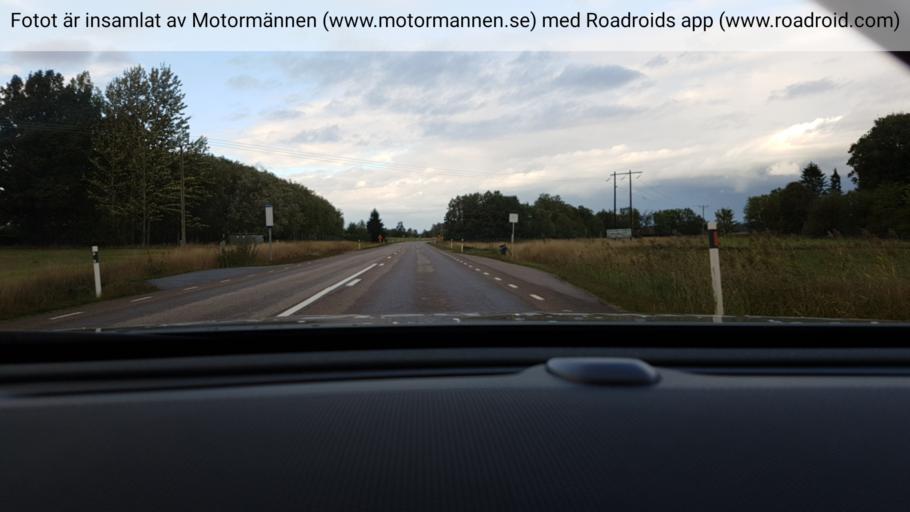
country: SE
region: Vaestra Goetaland
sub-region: Melleruds Kommun
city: Mellerud
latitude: 58.7153
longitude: 12.4562
